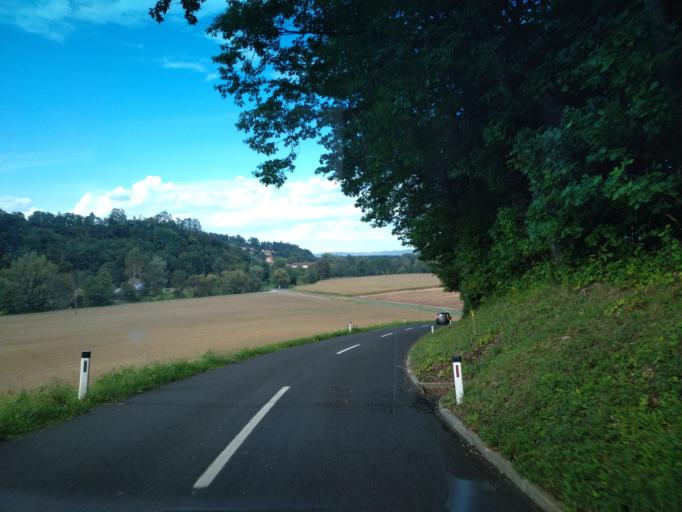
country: AT
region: Styria
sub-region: Politischer Bezirk Leibnitz
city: Leibnitz
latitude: 46.7875
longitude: 15.5225
